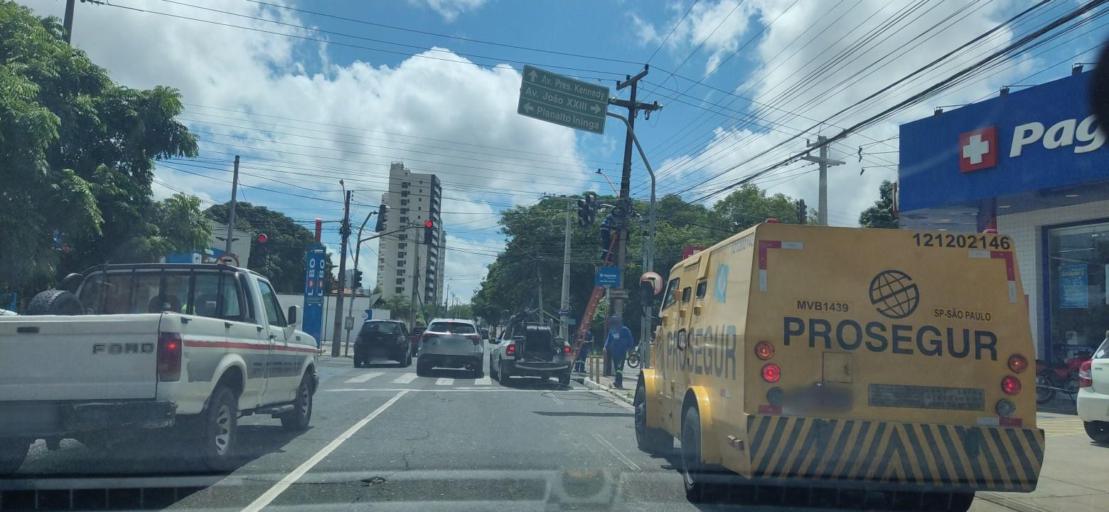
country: BR
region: Piaui
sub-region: Teresina
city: Teresina
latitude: -5.0647
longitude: -42.7848
